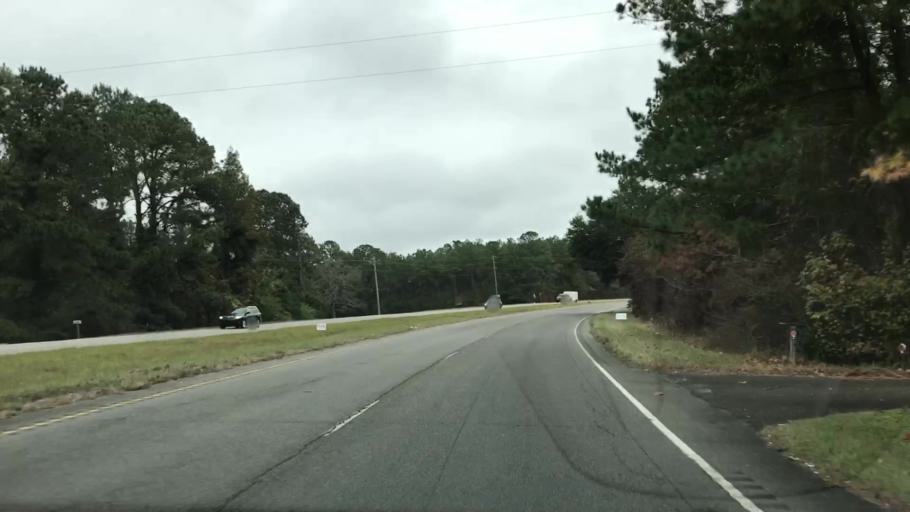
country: US
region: South Carolina
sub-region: Charleston County
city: Awendaw
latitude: 33.0371
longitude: -79.6167
